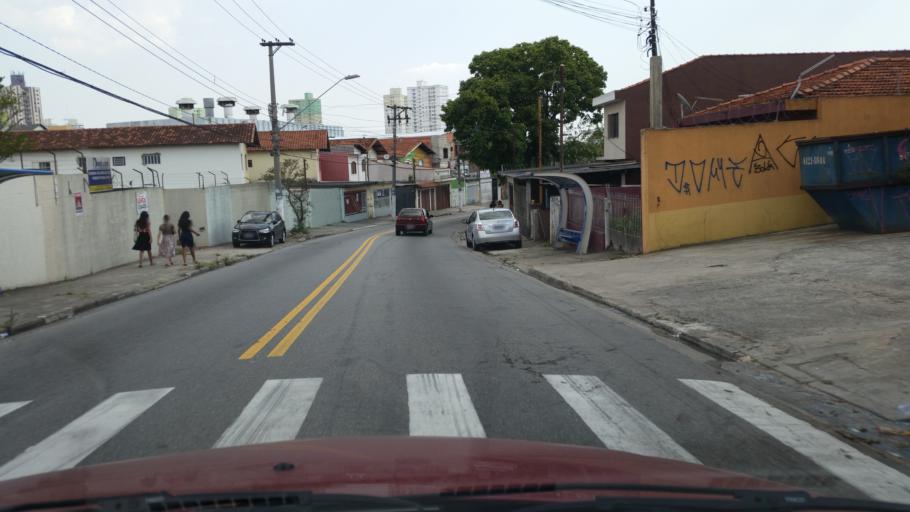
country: BR
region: Sao Paulo
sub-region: Santo Andre
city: Santo Andre
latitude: -23.6554
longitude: -46.5539
